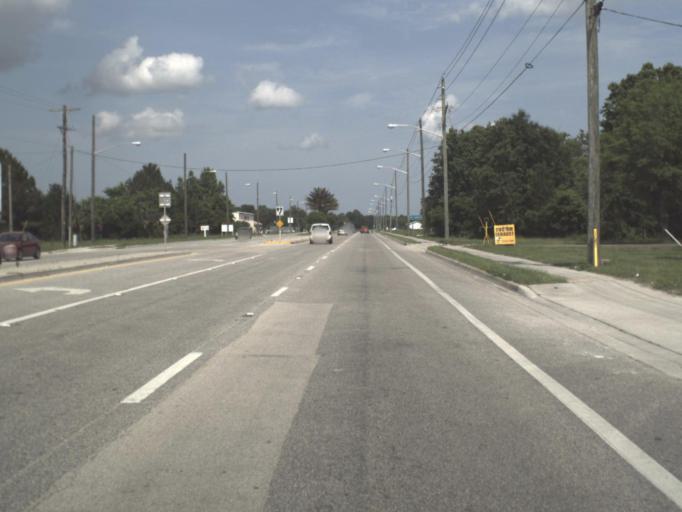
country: US
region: Florida
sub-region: Putnam County
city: East Palatka
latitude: 29.7143
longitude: -81.5055
